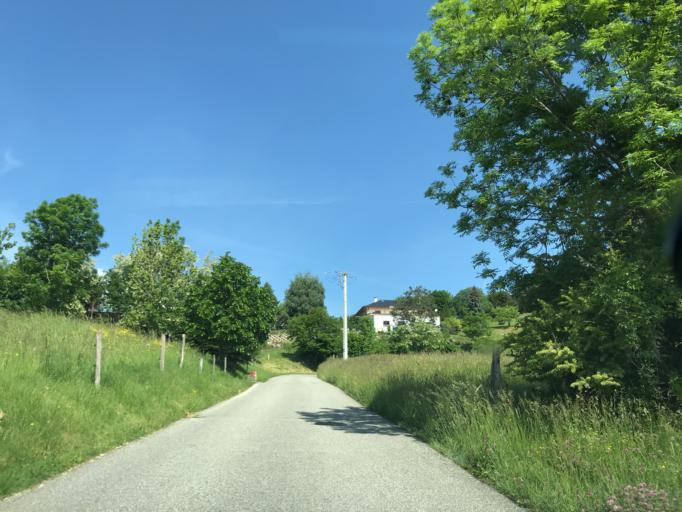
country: FR
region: Rhone-Alpes
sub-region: Departement de la Savoie
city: Vimines
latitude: 45.5498
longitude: 5.8741
